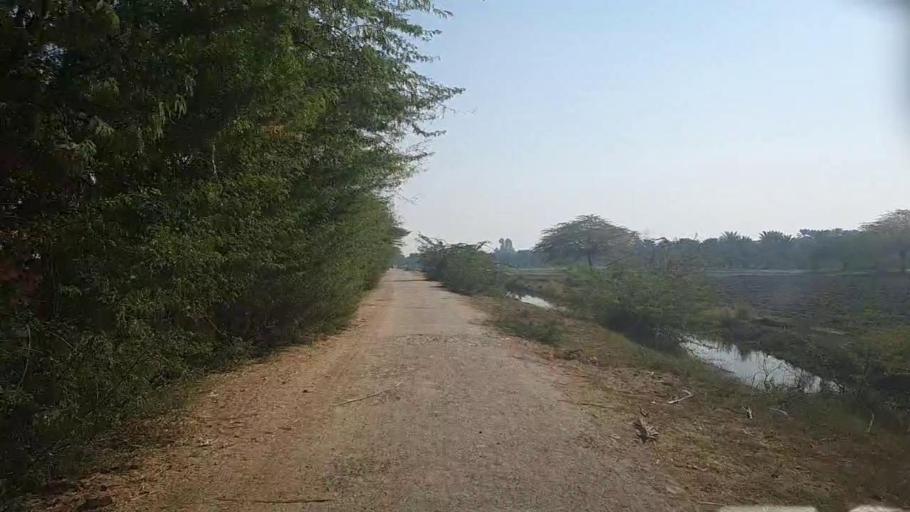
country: PK
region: Sindh
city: Kot Diji
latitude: 27.4366
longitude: 68.7134
